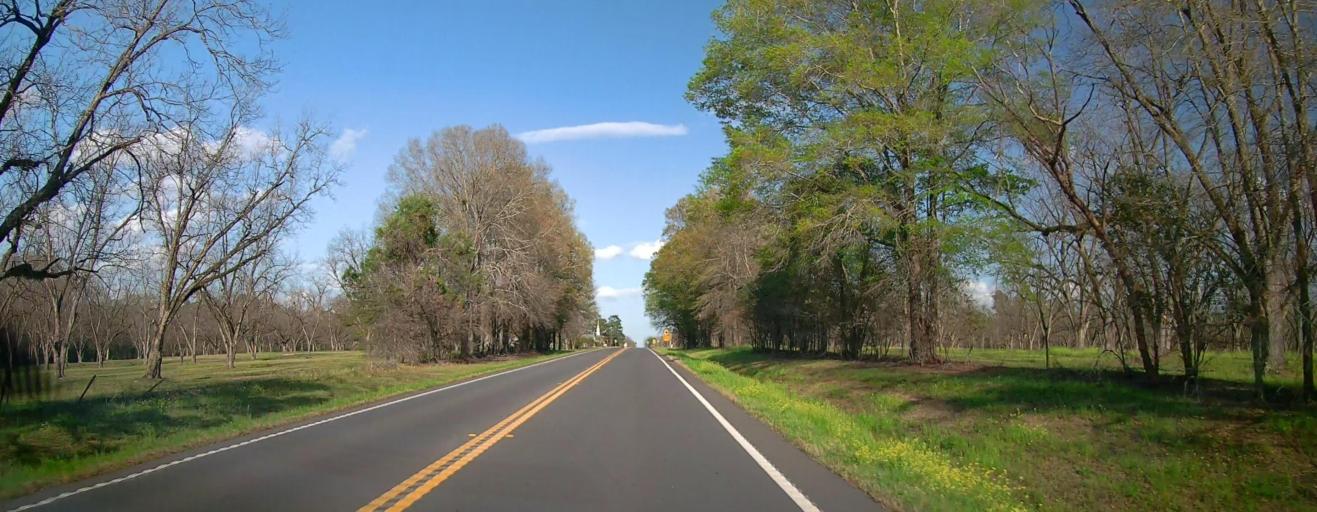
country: US
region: Georgia
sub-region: Montgomery County
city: Mount Vernon
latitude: 32.1951
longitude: -82.5095
